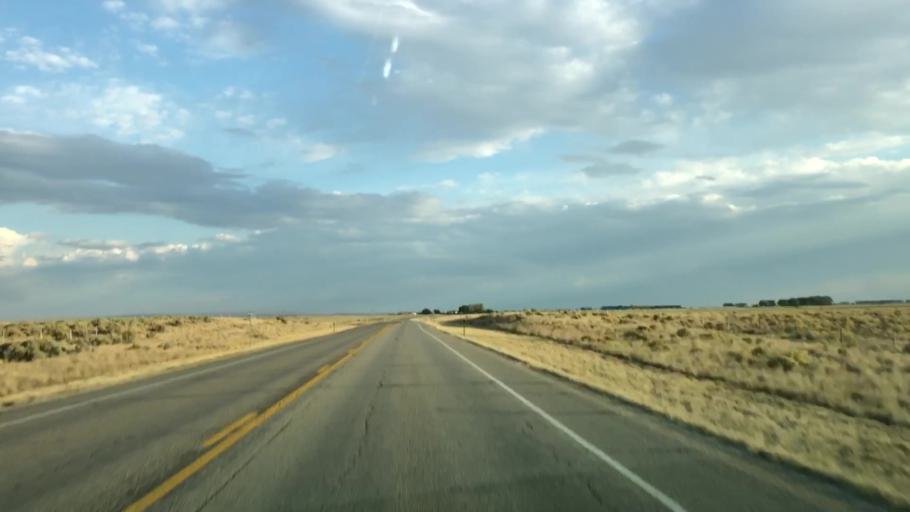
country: US
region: Wyoming
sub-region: Sweetwater County
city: North Rock Springs
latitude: 42.0919
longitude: -109.4417
